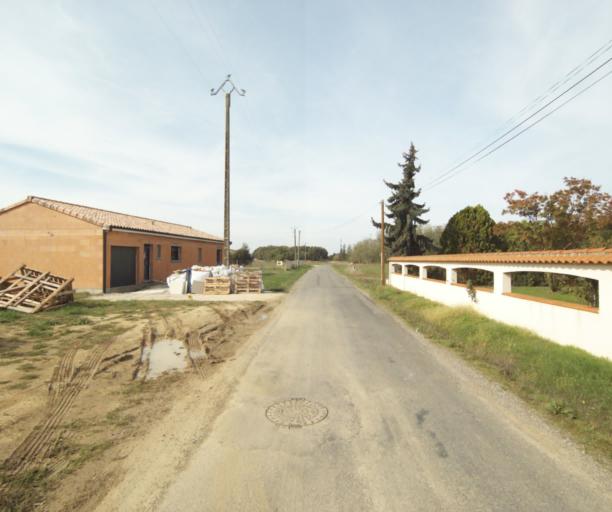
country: FR
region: Midi-Pyrenees
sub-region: Departement du Tarn-et-Garonne
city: Orgueil
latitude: 43.9083
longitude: 1.4042
